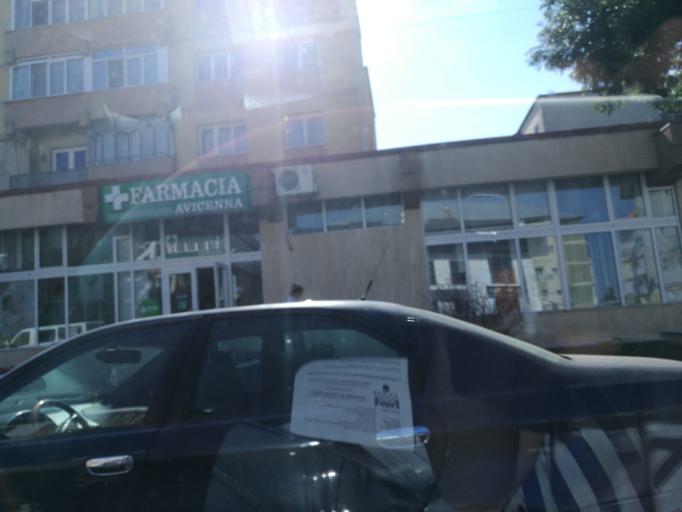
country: RO
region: Suceava
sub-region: Municipiul Suceava
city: Radauti
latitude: 47.8367
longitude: 25.9284
